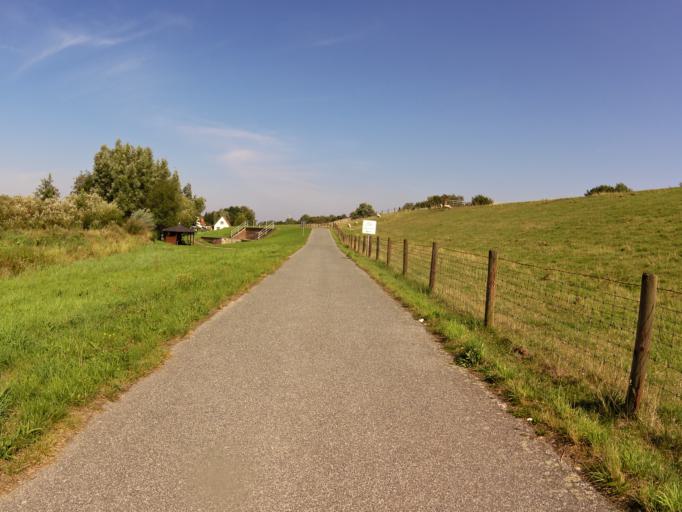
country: DE
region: Lower Saxony
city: Brake (Unterweser)
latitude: 53.2933
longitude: 8.4847
